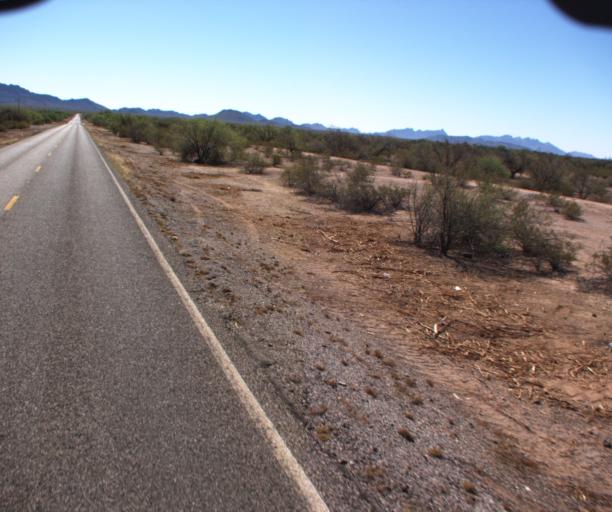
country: US
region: Arizona
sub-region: Pima County
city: Ajo
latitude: 32.3343
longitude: -112.7903
